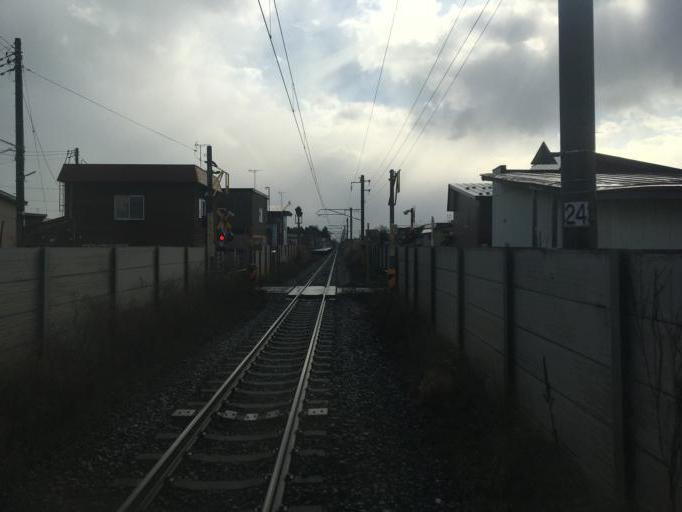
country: JP
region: Aomori
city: Aomori Shi
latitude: 40.8585
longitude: 140.6891
